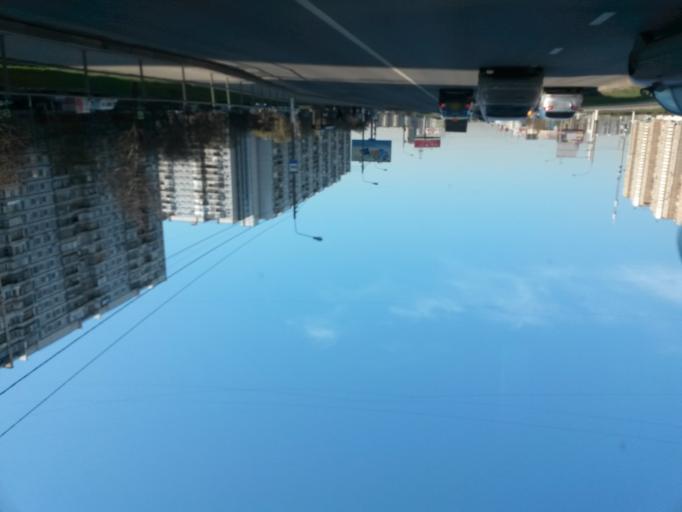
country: RU
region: Moscow
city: Brateyevo
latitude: 55.6337
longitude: 37.7504
